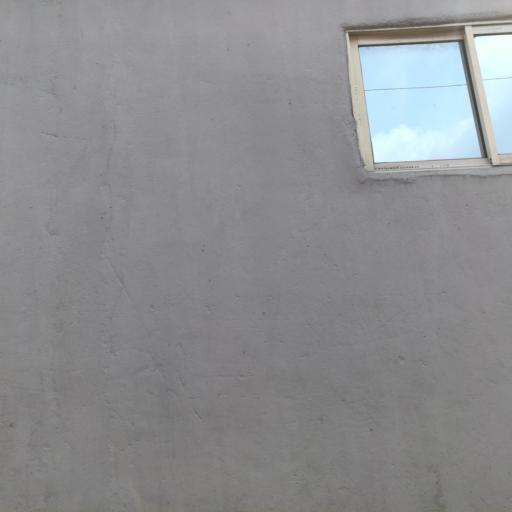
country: NG
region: Rivers
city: Port Harcourt
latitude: 4.8393
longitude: 7.0761
